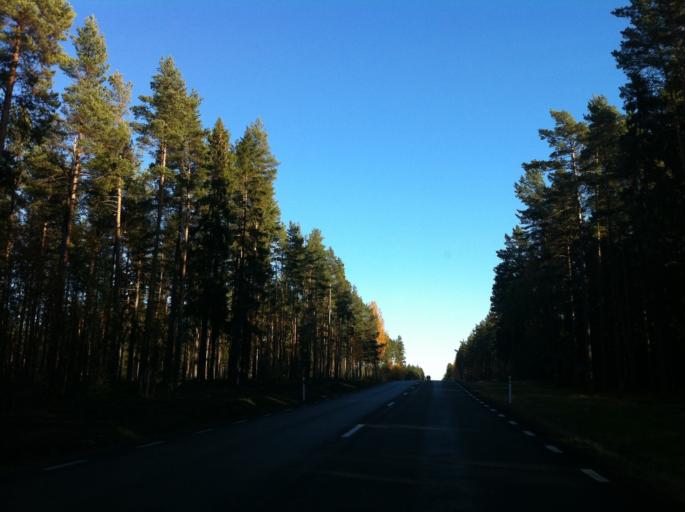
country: SE
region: Dalarna
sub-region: Rattviks Kommun
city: Vikarbyn
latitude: 60.9129
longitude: 14.8955
